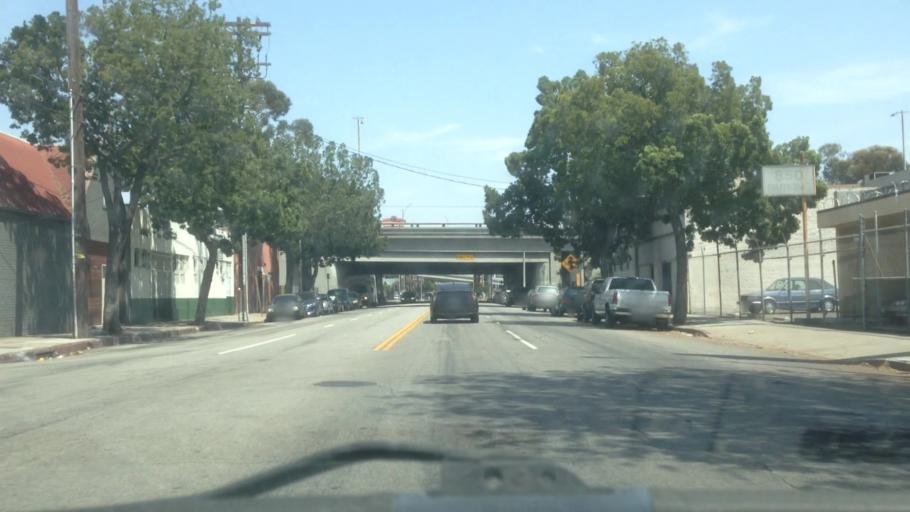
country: US
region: California
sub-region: Los Angeles County
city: Los Angeles
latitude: 34.0398
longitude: -118.2753
